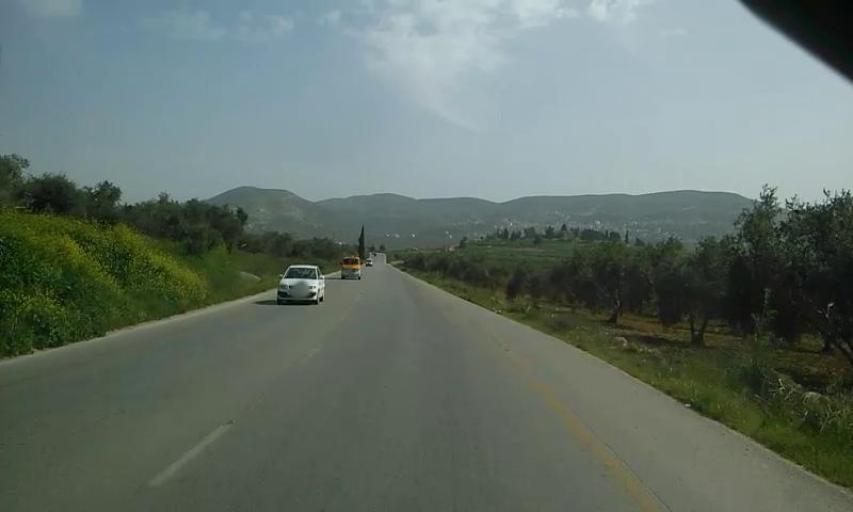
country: PS
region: West Bank
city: `Ajjah
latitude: 32.3442
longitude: 35.2016
